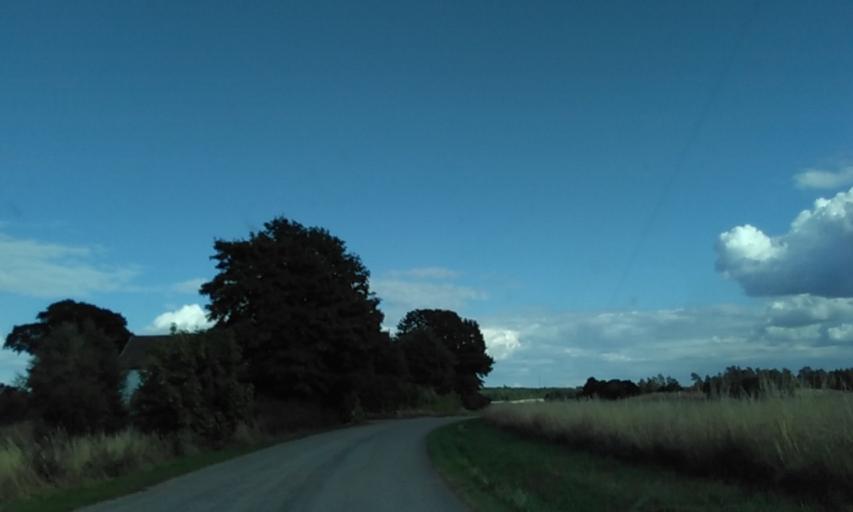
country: SE
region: Vaestra Goetaland
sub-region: Lidkopings Kommun
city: Lidkoping
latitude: 58.5737
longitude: 13.0284
